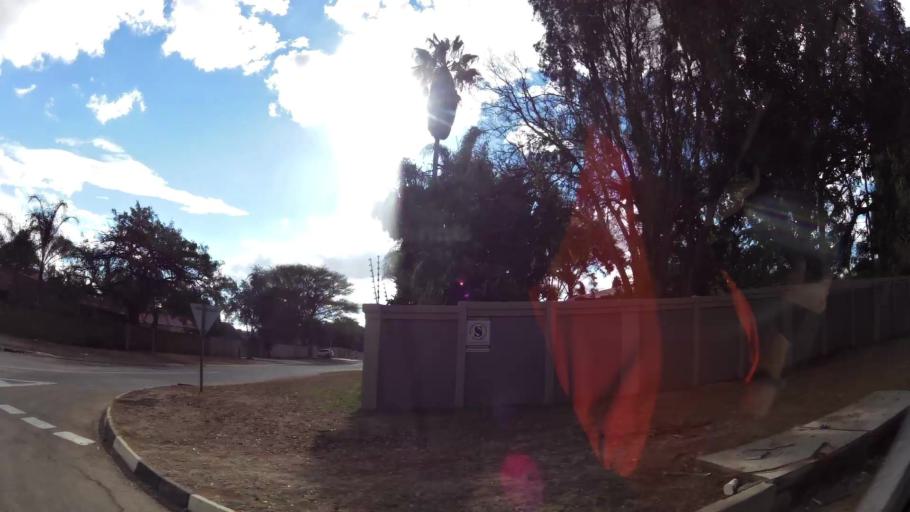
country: ZA
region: Limpopo
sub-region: Capricorn District Municipality
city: Polokwane
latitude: -23.8934
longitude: 29.4786
